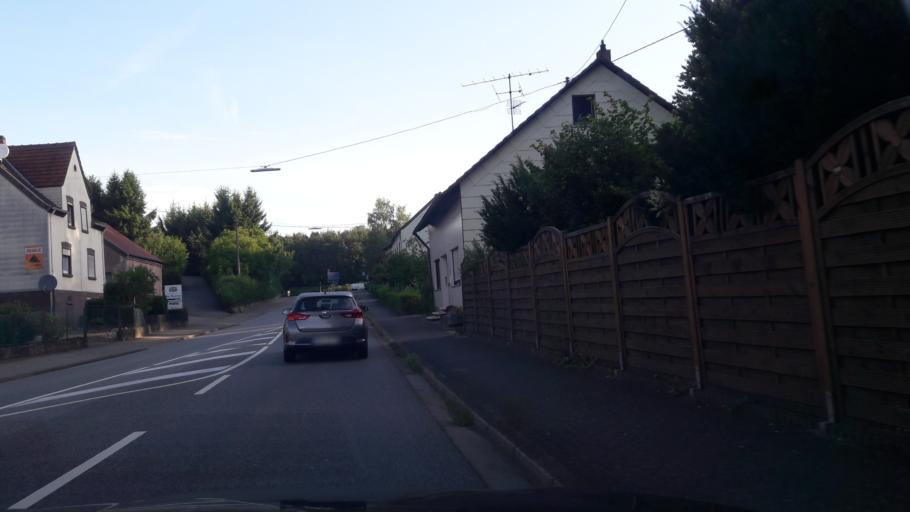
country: DE
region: Saarland
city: Heusweiler
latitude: 49.3462
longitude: 6.9354
